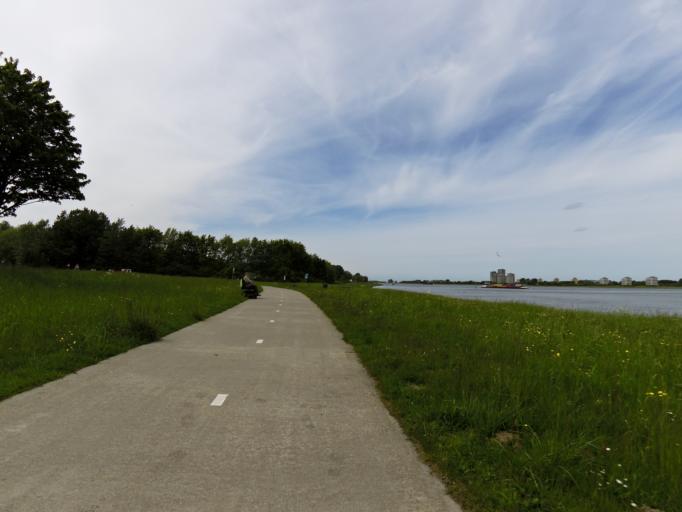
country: NL
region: South Holland
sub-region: Gemeente Maassluis
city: Maassluis
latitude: 51.9175
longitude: 4.2281
